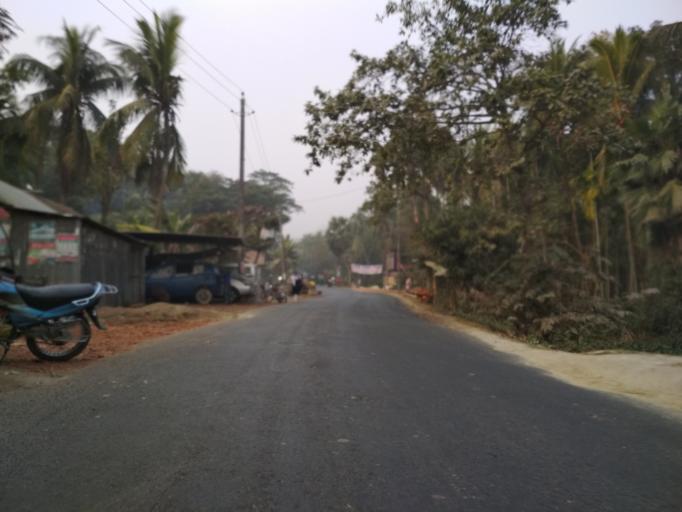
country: BD
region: Chittagong
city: Lakshmipur
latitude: 22.9260
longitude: 90.8339
